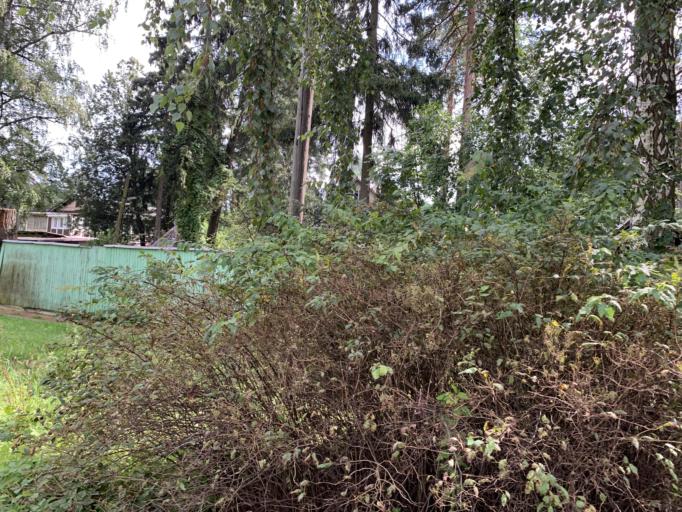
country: RU
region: Moskovskaya
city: Mamontovka
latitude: 55.9794
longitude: 37.8257
